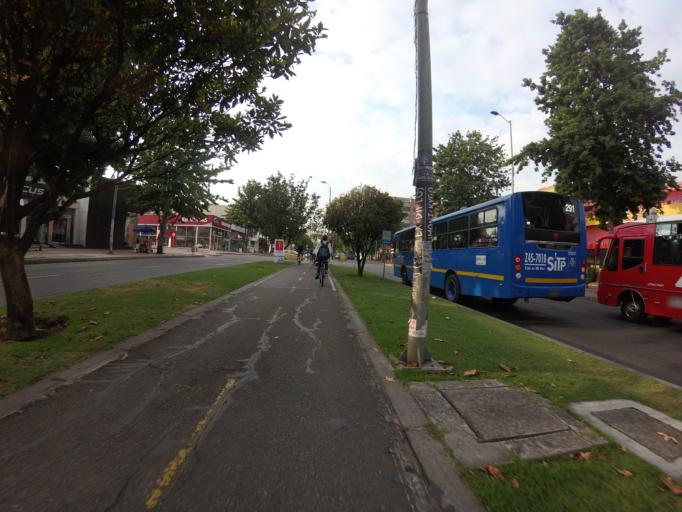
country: CO
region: Bogota D.C.
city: Barrio San Luis
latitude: 4.6937
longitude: -74.0509
